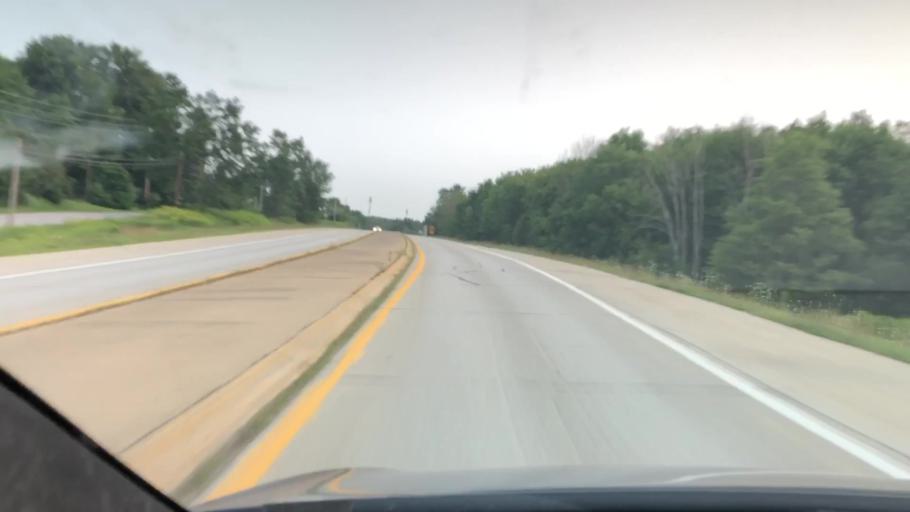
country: US
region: Pennsylvania
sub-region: Mercer County
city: Grove City
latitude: 41.2144
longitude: -79.9725
